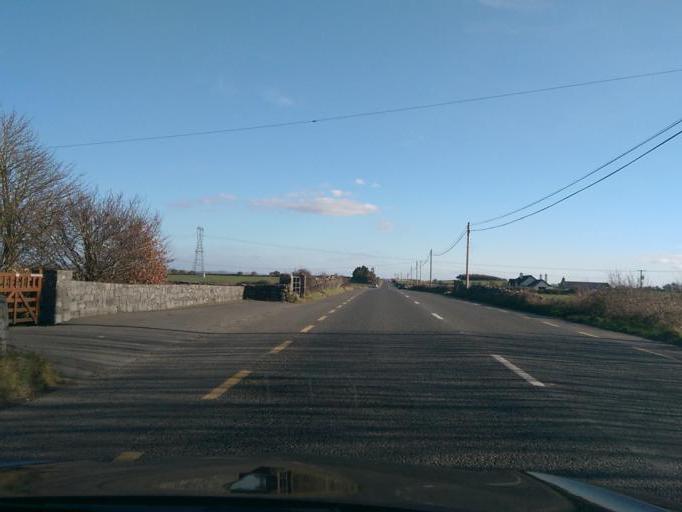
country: IE
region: Connaught
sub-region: County Galway
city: Oranmore
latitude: 53.2016
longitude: -8.8620
